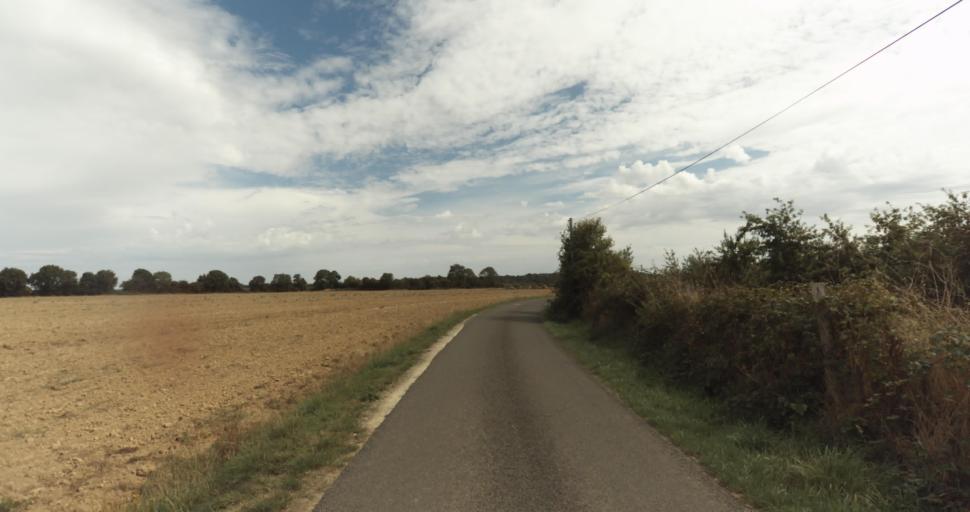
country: FR
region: Lower Normandy
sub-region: Departement du Calvados
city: Orbec
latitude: 48.9279
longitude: 0.3540
